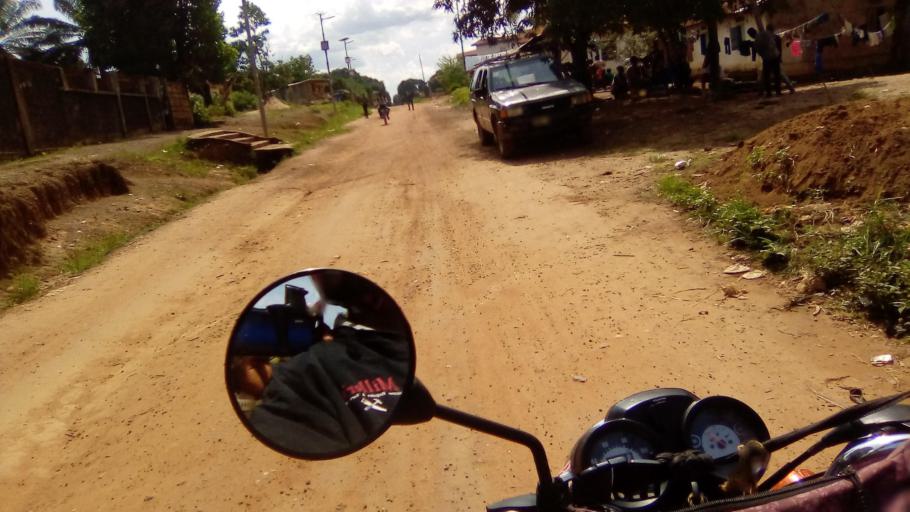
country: SL
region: Southern Province
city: Bo
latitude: 7.9497
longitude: -11.7225
